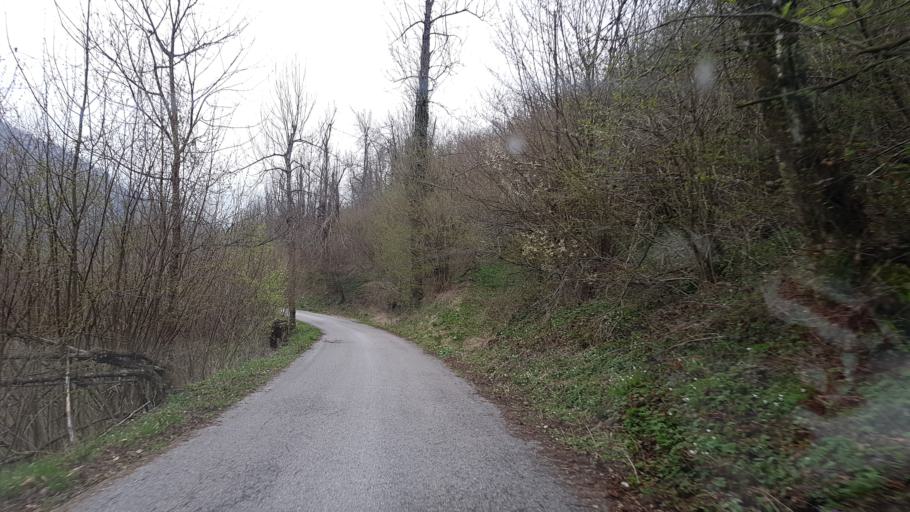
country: IT
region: Friuli Venezia Giulia
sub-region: Provincia di Udine
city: Faedis
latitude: 46.1855
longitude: 13.3950
